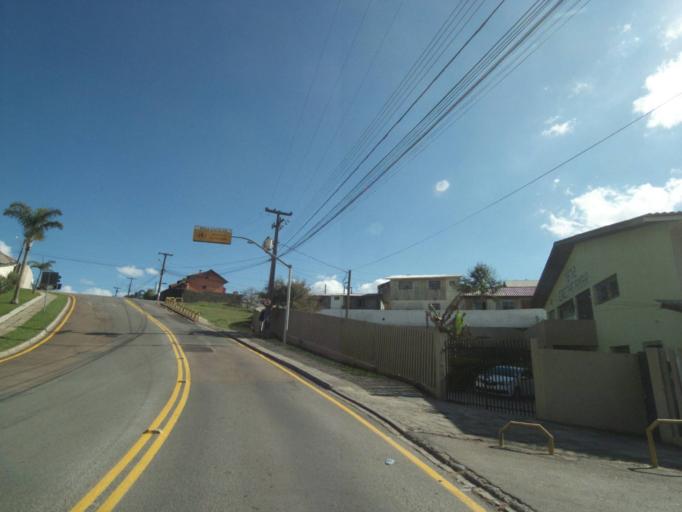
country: BR
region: Parana
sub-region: Curitiba
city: Curitiba
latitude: -25.3865
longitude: -49.2586
